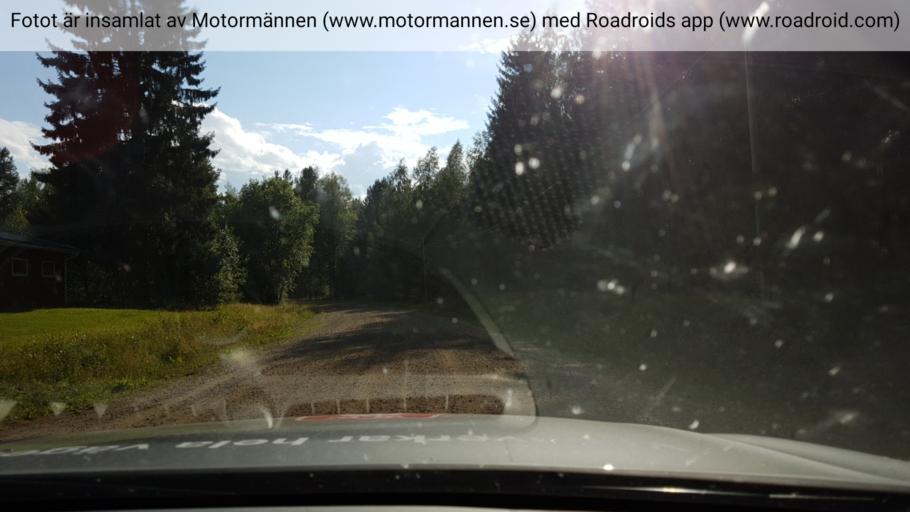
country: SE
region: Vaesternorrland
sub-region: Solleftea Kommun
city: As
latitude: 63.7317
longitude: 16.1371
